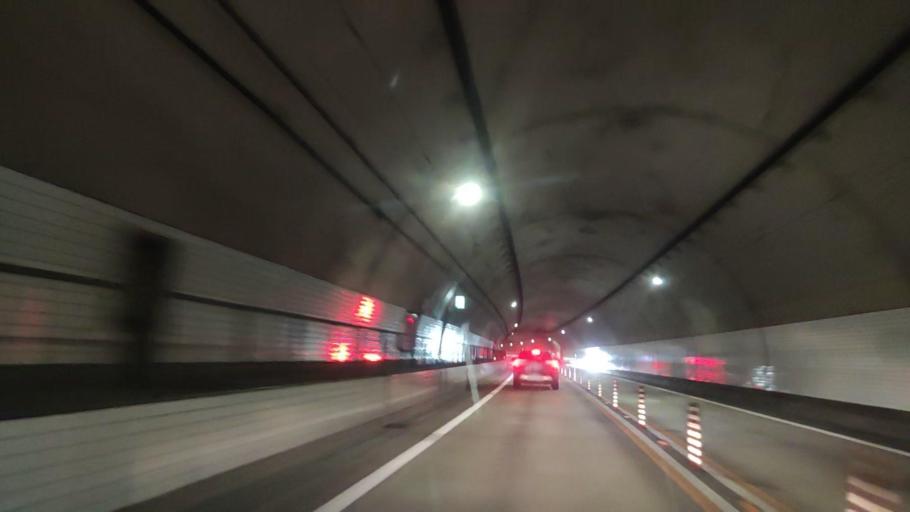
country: JP
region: Kyoto
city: Miyazu
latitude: 35.5572
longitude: 135.1254
